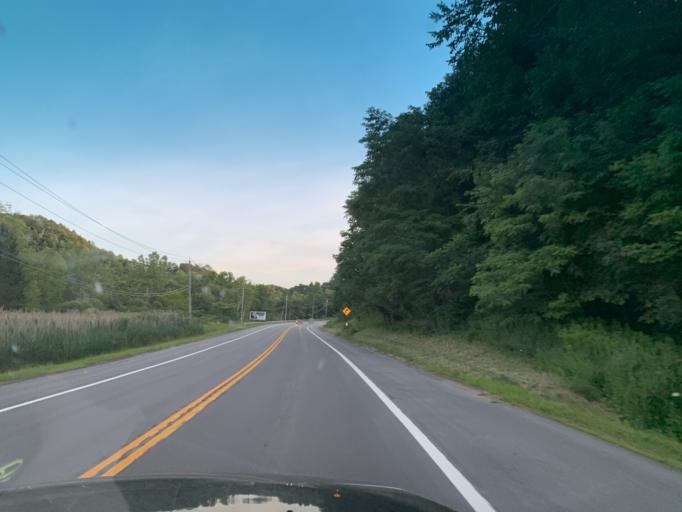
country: US
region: New York
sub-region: Oneida County
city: Chadwicks
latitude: 42.9495
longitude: -75.2444
